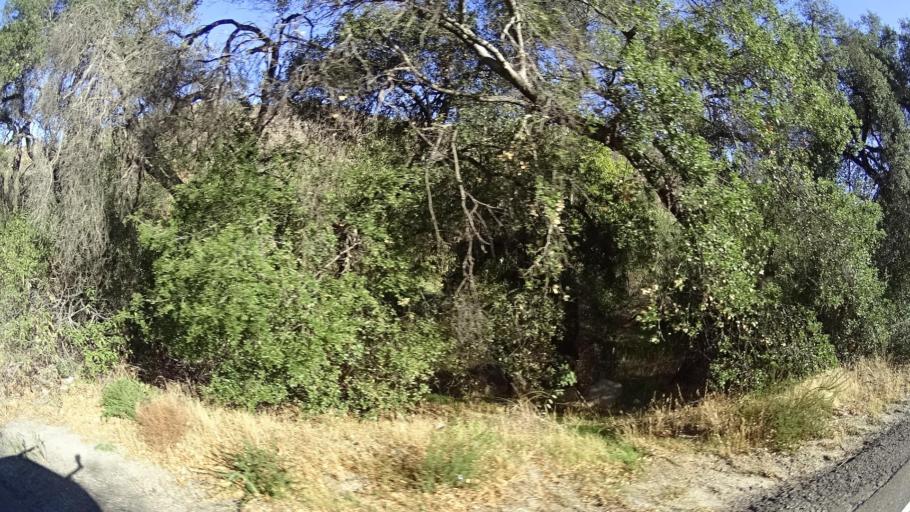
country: US
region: California
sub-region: San Diego County
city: Jamul
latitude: 32.6544
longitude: -116.7946
